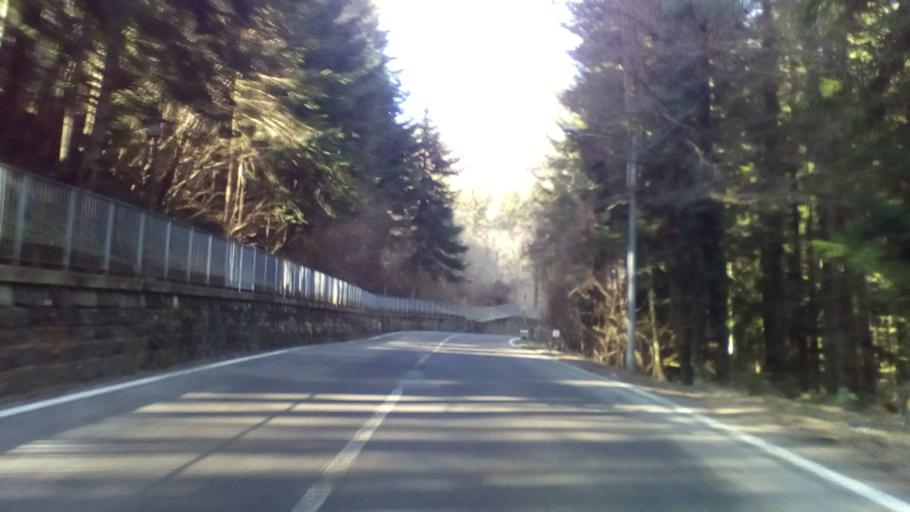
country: IT
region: Emilia-Romagna
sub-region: Provincia di Modena
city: Pievepelago
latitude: 44.2083
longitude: 10.6118
